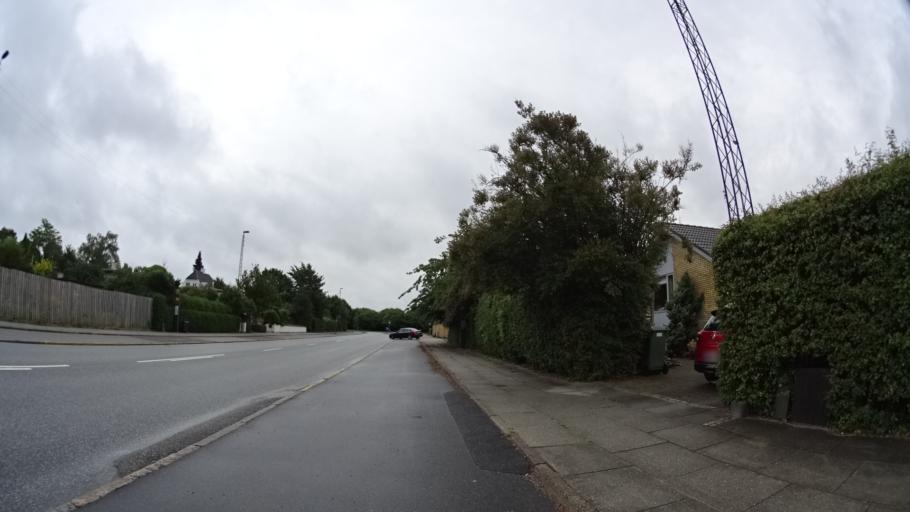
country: DK
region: Central Jutland
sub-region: Arhus Kommune
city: Arhus
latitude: 56.1278
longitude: 10.1836
